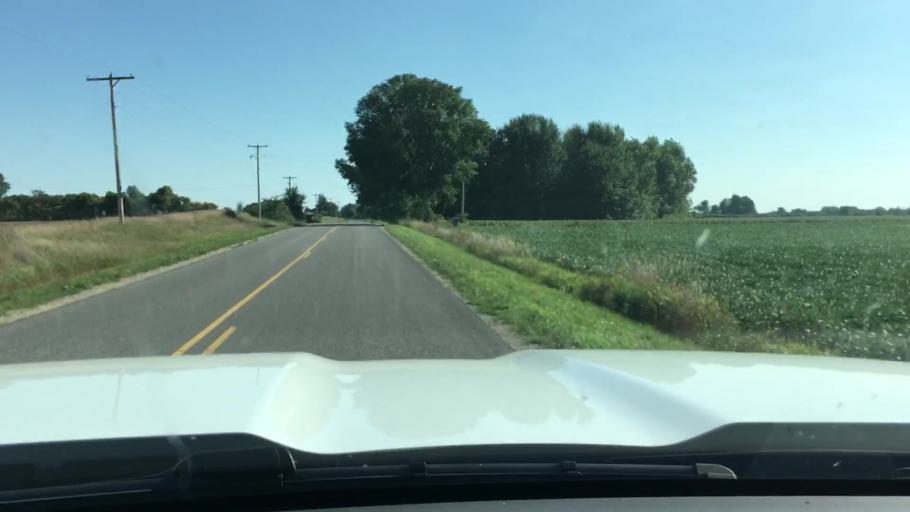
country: US
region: Michigan
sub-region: Muskegon County
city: Ravenna
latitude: 43.2421
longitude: -85.9180
